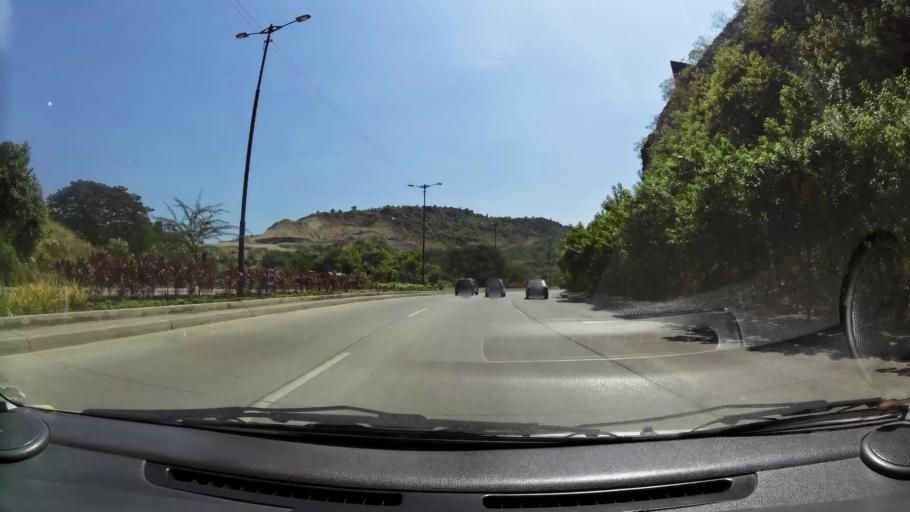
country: EC
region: Guayas
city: Guayaquil
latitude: -2.1883
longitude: -79.9324
